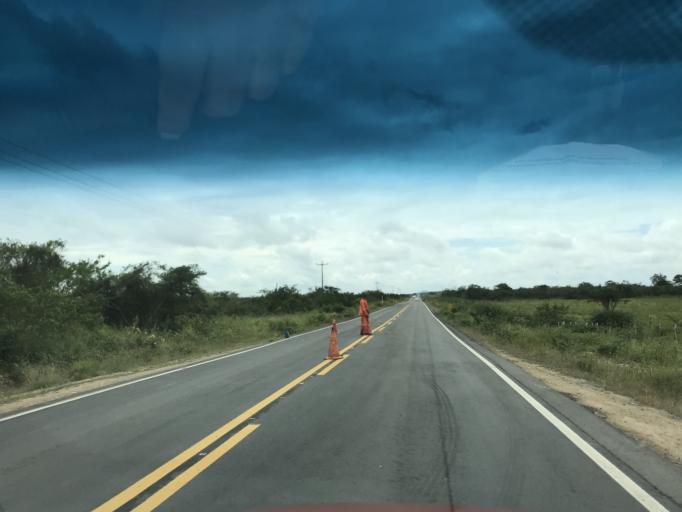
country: BR
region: Bahia
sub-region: Castro Alves
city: Castro Alves
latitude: -12.6841
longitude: -39.3080
